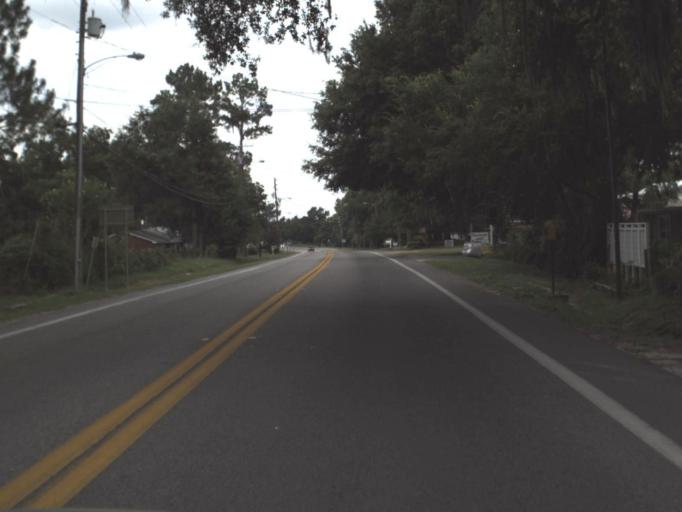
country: US
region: Florida
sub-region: Hamilton County
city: Jasper
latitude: 30.5119
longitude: -82.9463
